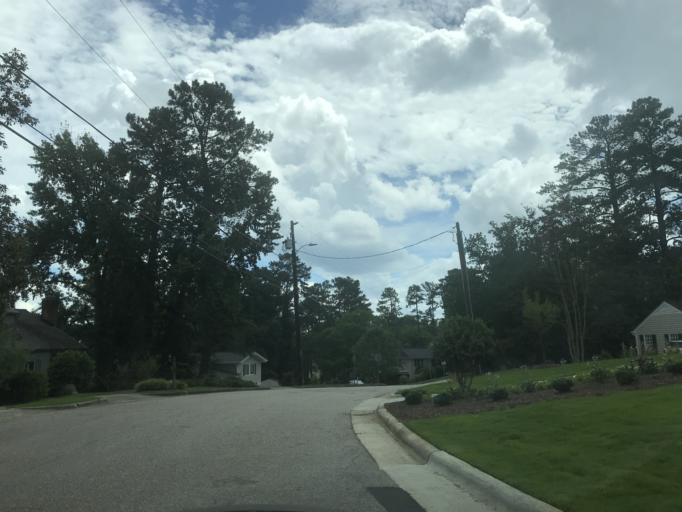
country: US
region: North Carolina
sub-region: Wake County
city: West Raleigh
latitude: 35.8280
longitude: -78.6387
